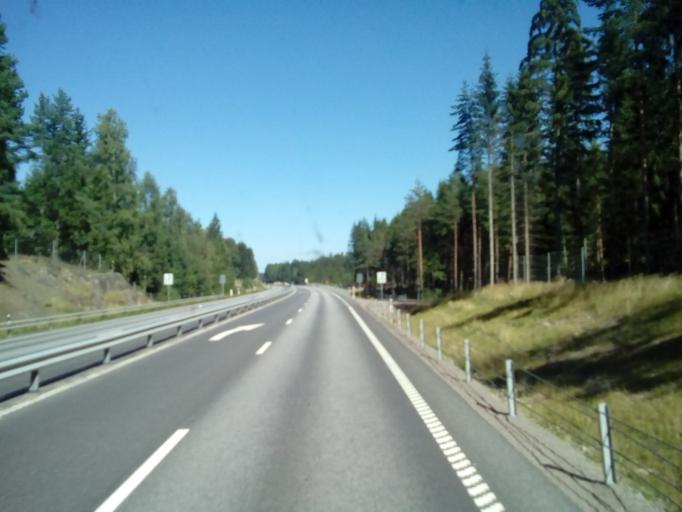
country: SE
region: OEstergoetland
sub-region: Kinda Kommun
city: Rimforsa
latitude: 58.0911
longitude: 15.6563
